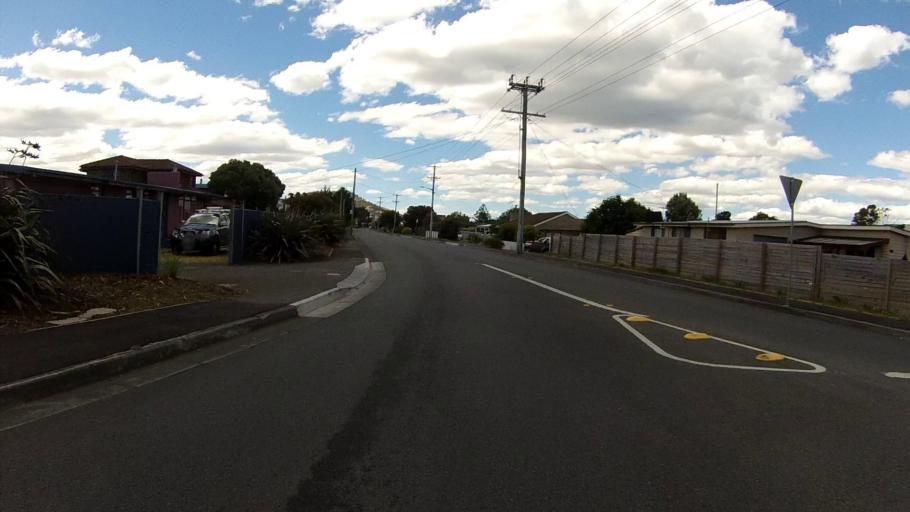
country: AU
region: Tasmania
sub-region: Clarence
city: Lauderdale
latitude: -42.9050
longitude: 147.4931
